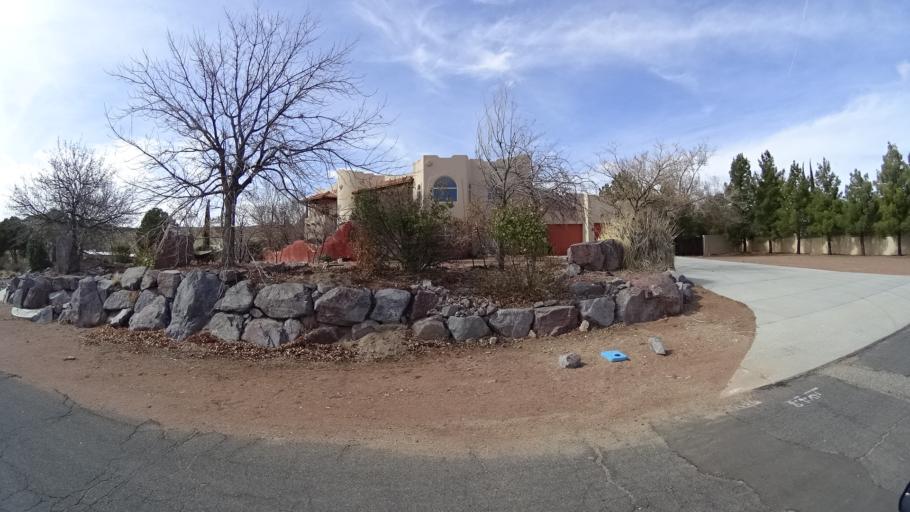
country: US
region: Arizona
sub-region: Mohave County
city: New Kingman-Butler
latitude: 35.2342
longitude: -114.0535
